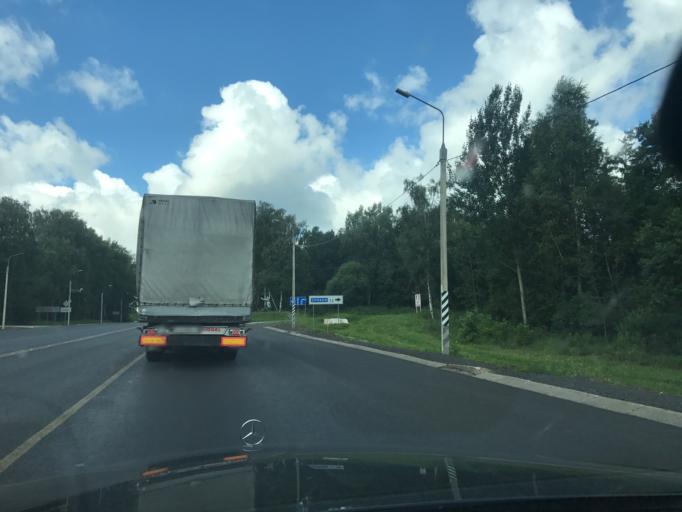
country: RU
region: Smolensk
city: Golynki
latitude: 54.7020
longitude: 31.1861
